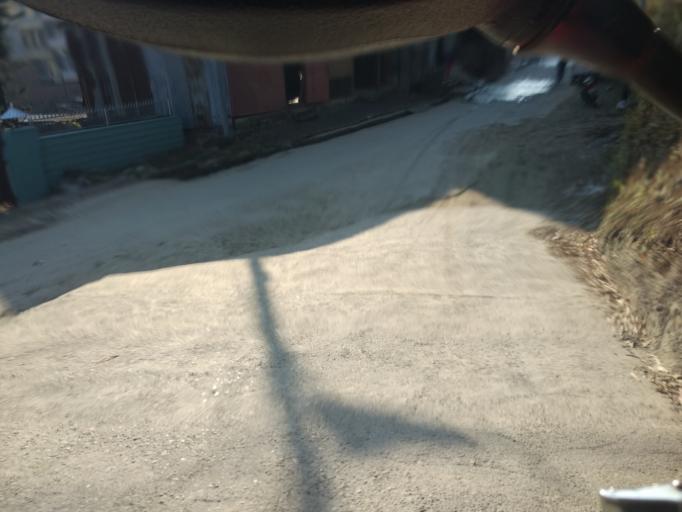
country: NP
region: Western Region
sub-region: Gandaki Zone
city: Pokhara
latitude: 28.2389
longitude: 83.9854
